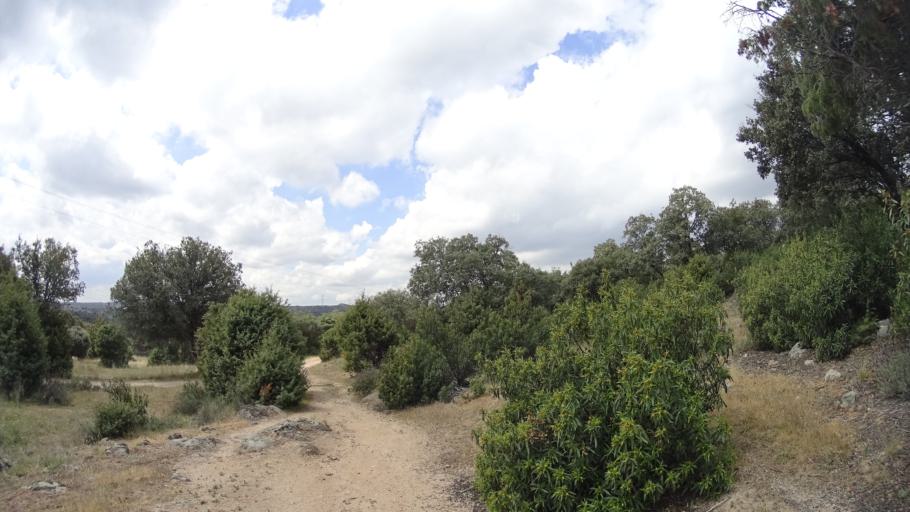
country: ES
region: Madrid
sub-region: Provincia de Madrid
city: Hoyo de Manzanares
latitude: 40.6179
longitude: -3.8946
